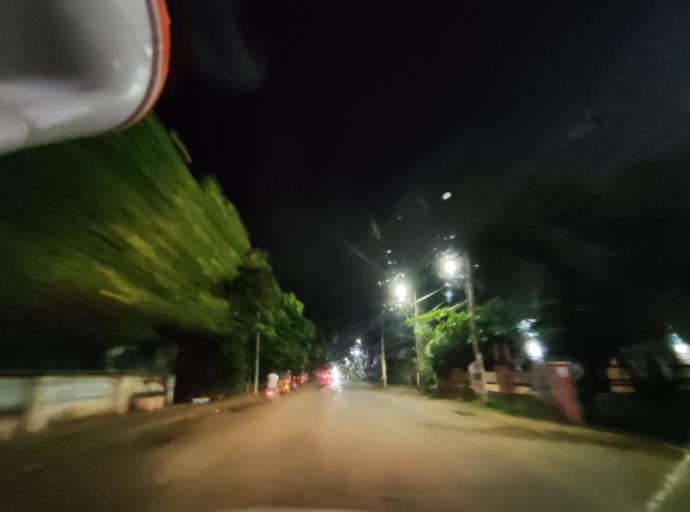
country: IN
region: Kerala
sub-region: Thiruvananthapuram
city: Thiruvananthapuram
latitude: 8.4651
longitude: 76.9251
